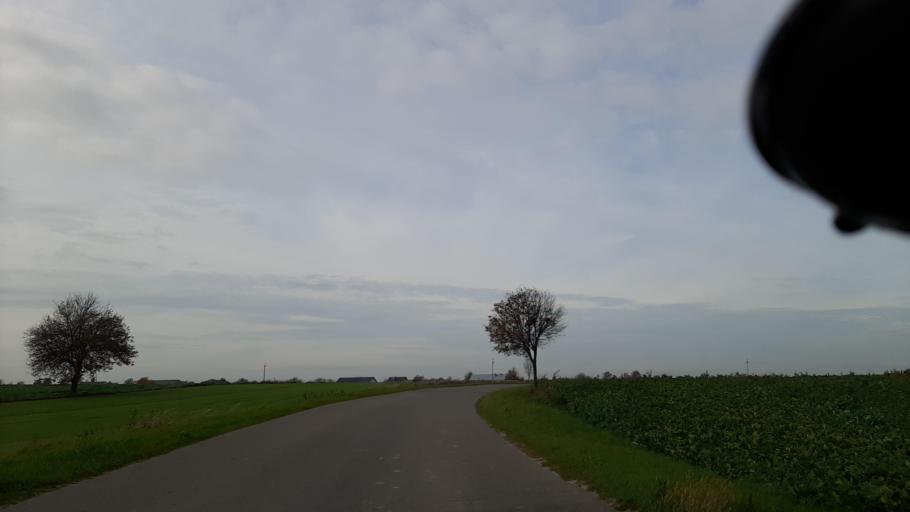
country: PL
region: Lublin Voivodeship
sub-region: Powiat lubelski
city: Garbow
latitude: 51.3850
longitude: 22.3723
